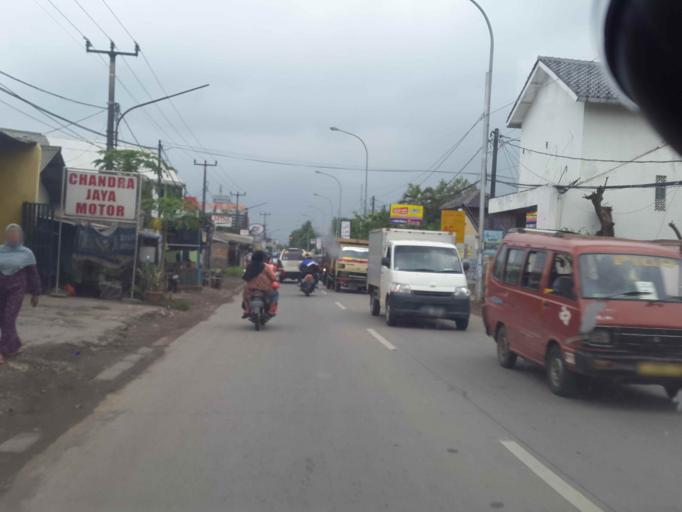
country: ID
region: West Java
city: Cikarang
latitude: -6.2747
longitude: 107.1729
